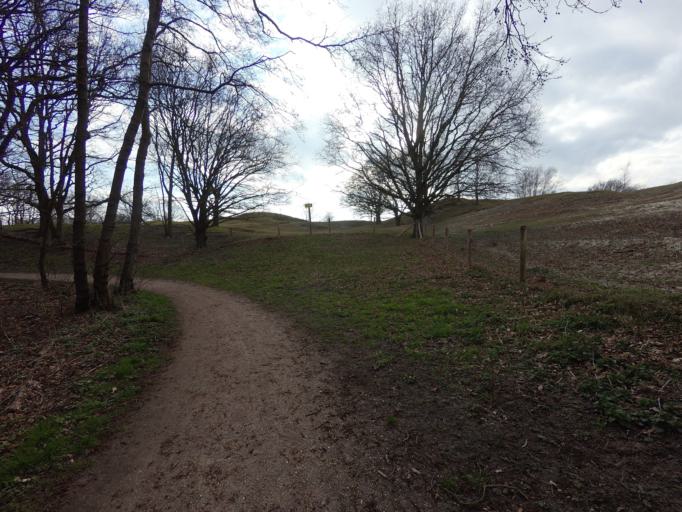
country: NL
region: Zeeland
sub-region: Schouwen-Duiveland
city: Burgh
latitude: 51.6955
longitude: 3.7319
